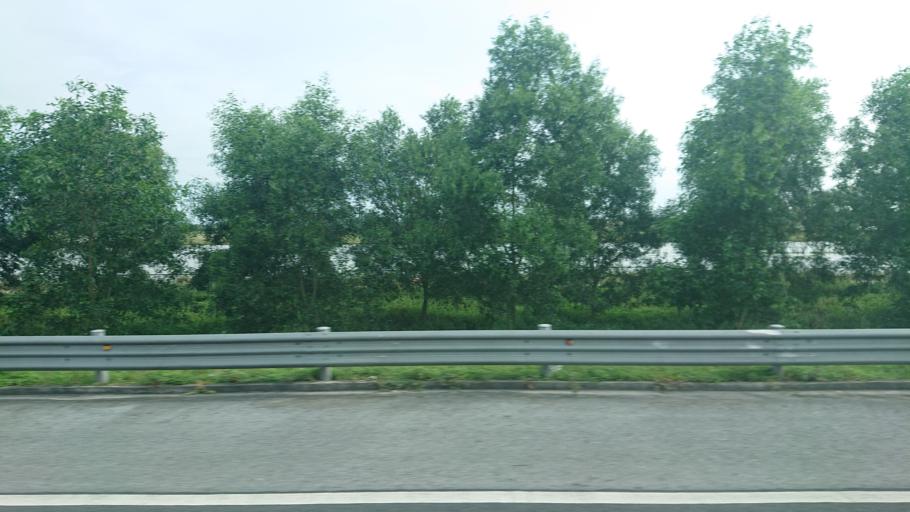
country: VN
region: Hai Phong
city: An Lao
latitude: 20.7967
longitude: 106.5423
